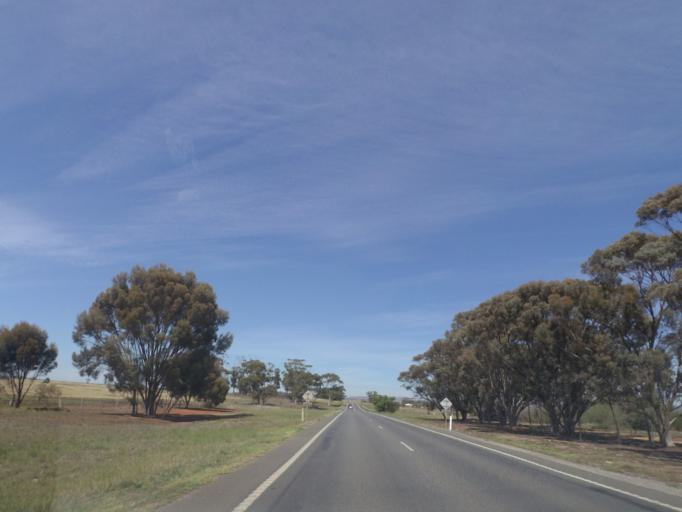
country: AU
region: Victoria
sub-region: Moorabool
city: Bacchus Marsh
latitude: -37.7957
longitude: 144.4130
